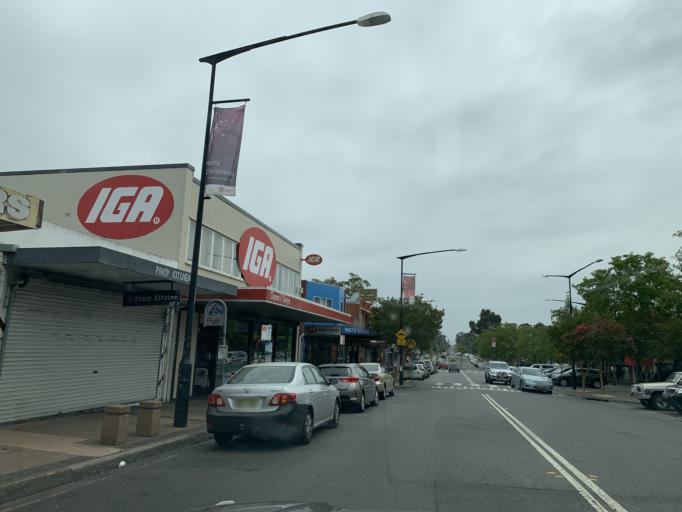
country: AU
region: New South Wales
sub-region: Blacktown
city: Doonside
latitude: -33.7633
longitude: 150.8694
